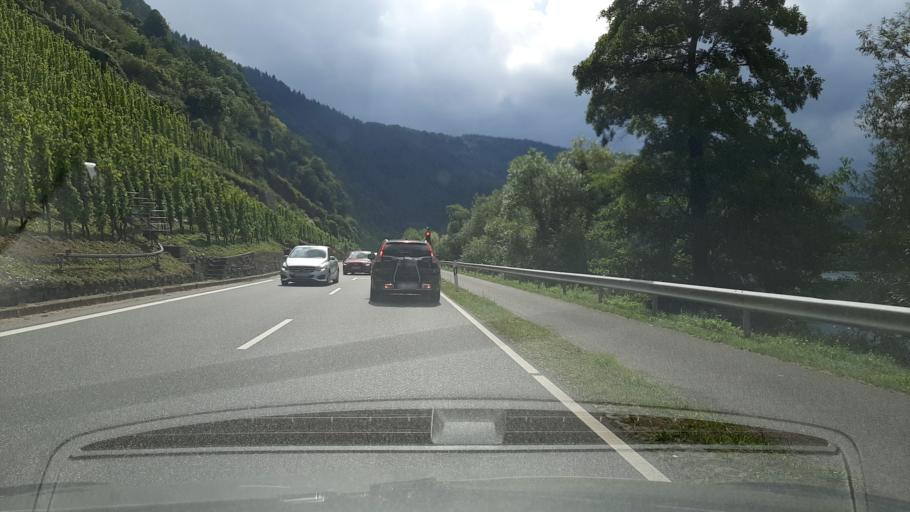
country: DE
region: Rheinland-Pfalz
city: Starkenburg
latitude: 49.9600
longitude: 7.1344
